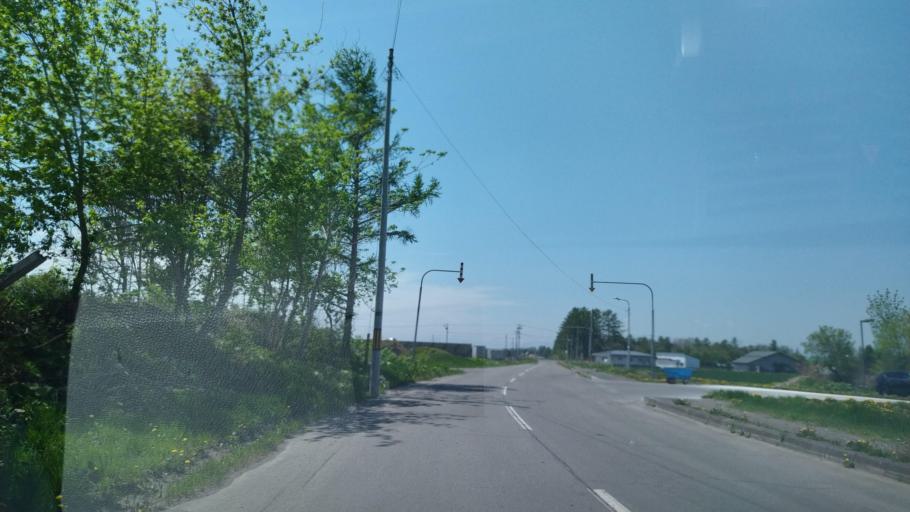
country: JP
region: Hokkaido
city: Otofuke
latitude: 43.2279
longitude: 143.2869
